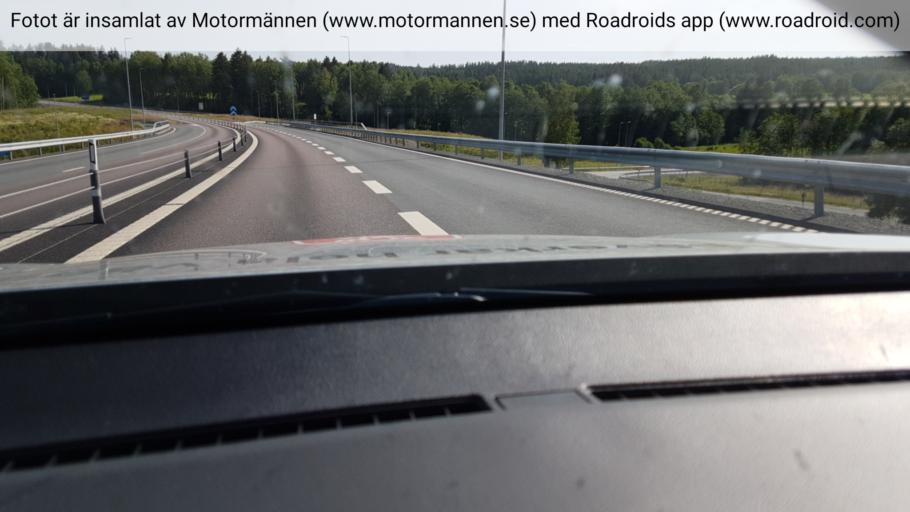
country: SE
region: Joenkoeping
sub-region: Aneby Kommun
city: Aneby
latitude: 57.8187
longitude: 14.8607
